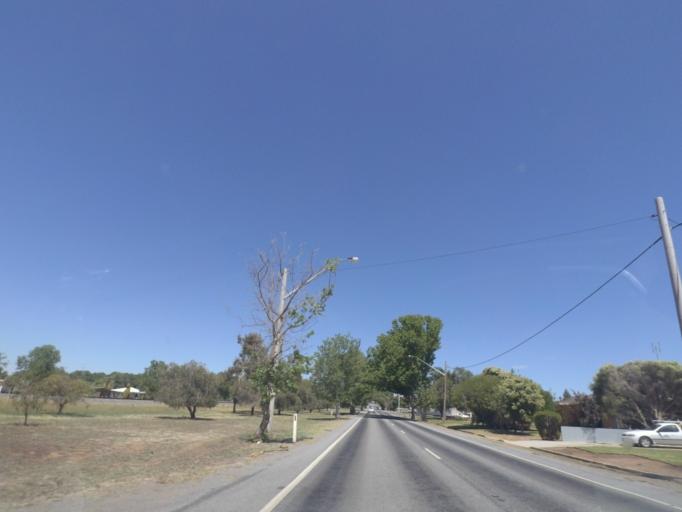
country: AU
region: New South Wales
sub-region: Narrandera
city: Narrandera
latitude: -34.7396
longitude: 146.5651
